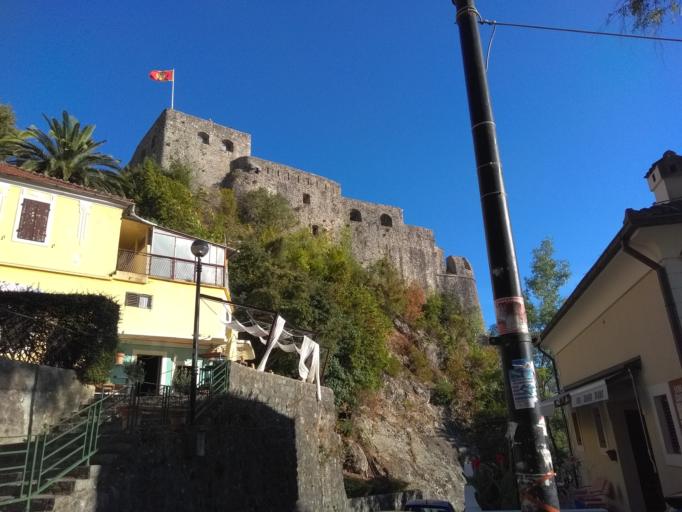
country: ME
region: Herceg Novi
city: Herceg-Novi
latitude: 42.4505
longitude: 18.5359
